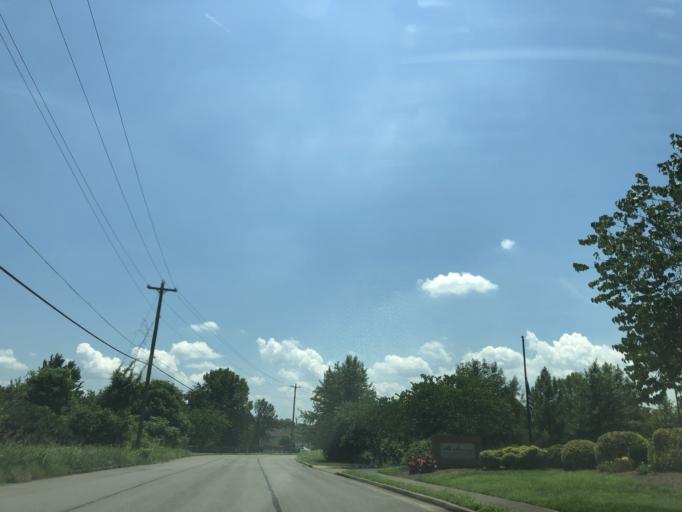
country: US
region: Tennessee
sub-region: Davidson County
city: Lakewood
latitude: 36.1810
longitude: -86.6373
